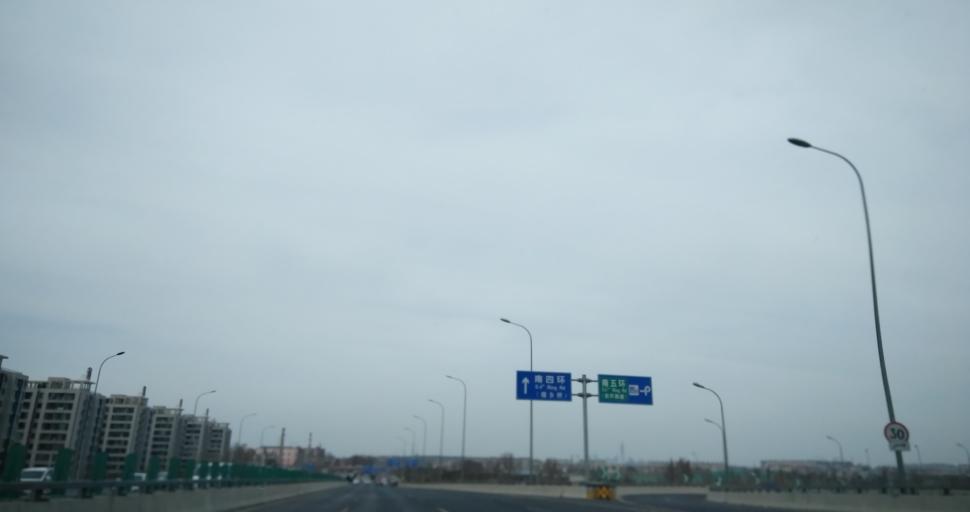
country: CN
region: Beijing
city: Yinghai
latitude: 39.7863
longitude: 116.4248
